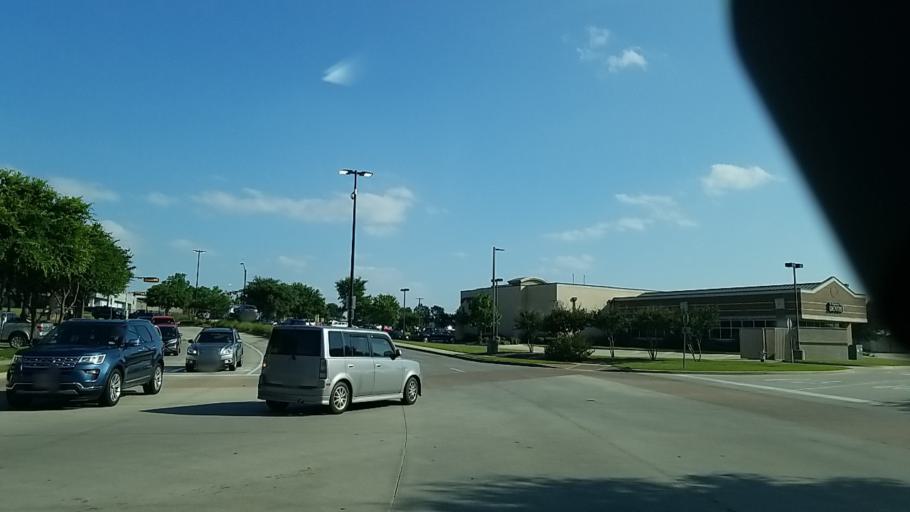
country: US
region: Texas
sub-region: Denton County
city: Copper Canyon
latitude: 33.0744
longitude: -97.0800
